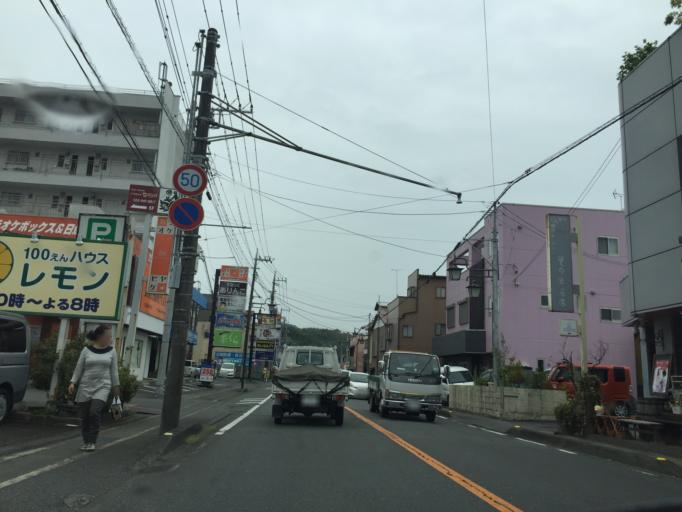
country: JP
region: Shizuoka
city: Mishima
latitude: 35.0379
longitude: 138.9471
